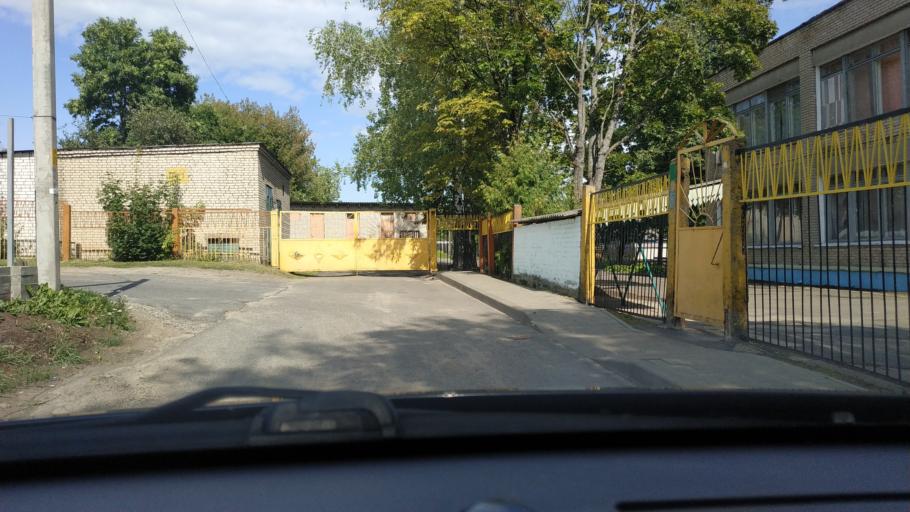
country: BY
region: Mogilev
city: Buynichy
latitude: 53.9004
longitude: 30.2928
